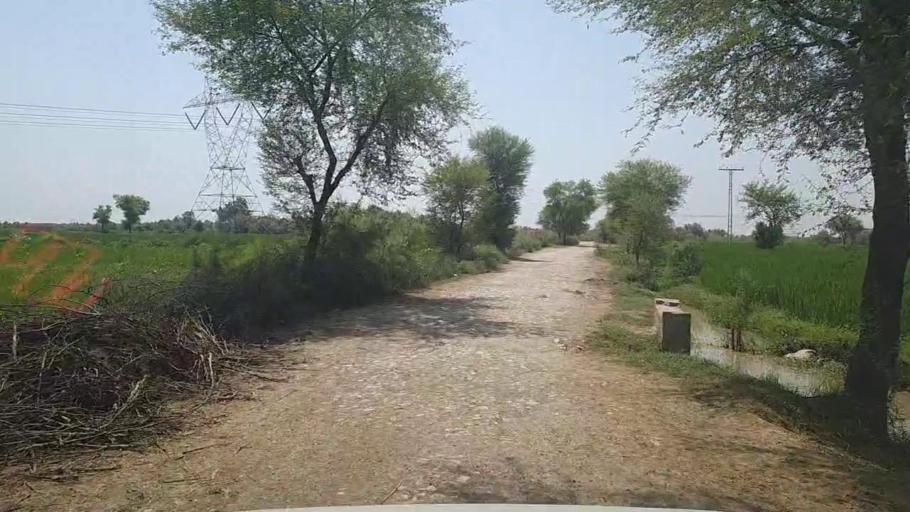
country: PK
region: Sindh
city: Kandhkot
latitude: 28.3148
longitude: 69.3620
